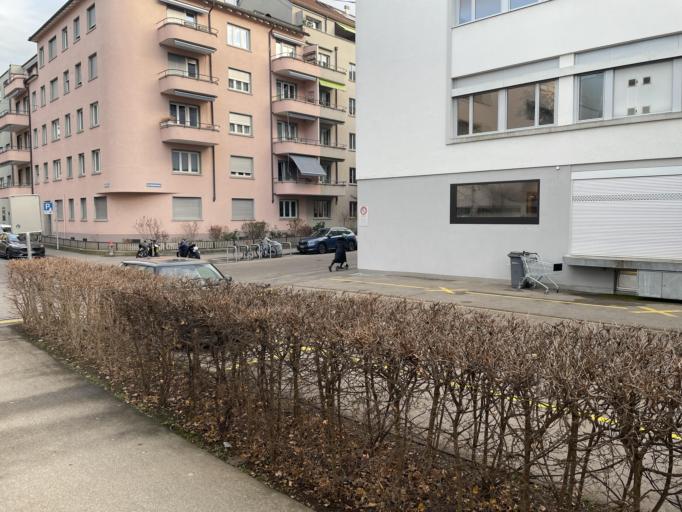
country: CH
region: Zurich
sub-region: Bezirk Zuerich
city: Zuerich (Kreis 3) / Alt-Wiedikon
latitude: 47.3596
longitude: 8.5213
